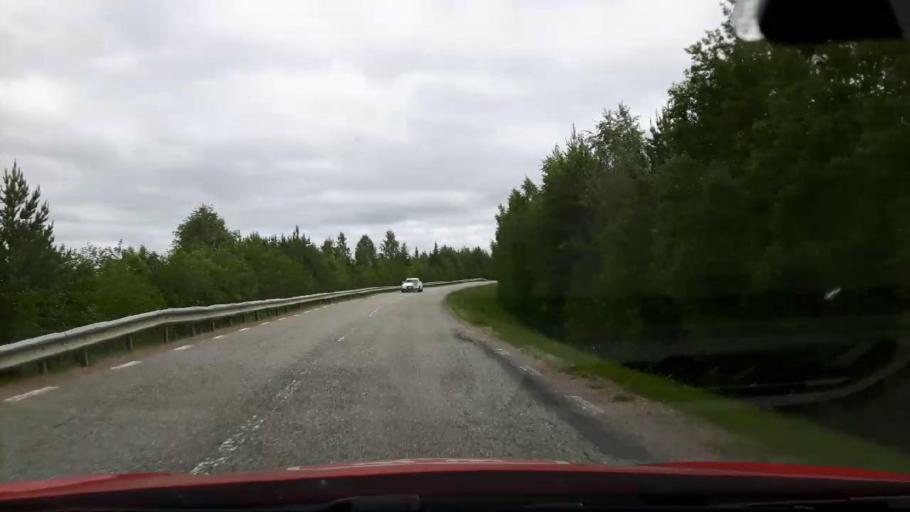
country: SE
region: Jaemtland
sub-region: Ragunda Kommun
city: Hammarstrand
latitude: 63.0422
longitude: 16.3896
